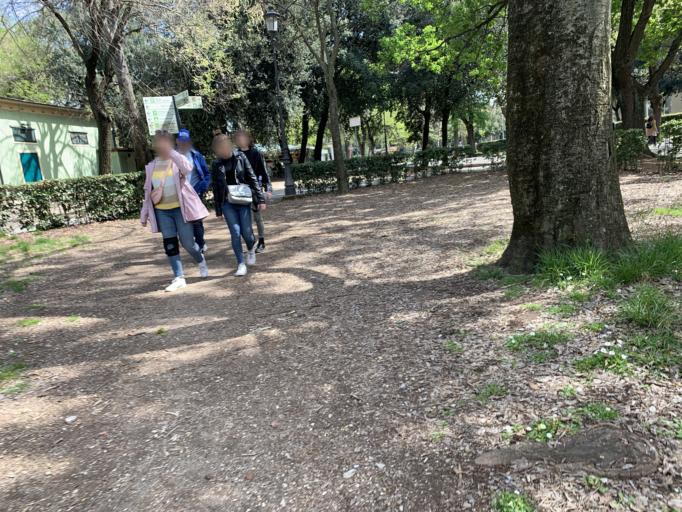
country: IT
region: Latium
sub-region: Citta metropolitana di Roma Capitale
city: Rome
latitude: 41.9116
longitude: 12.4873
